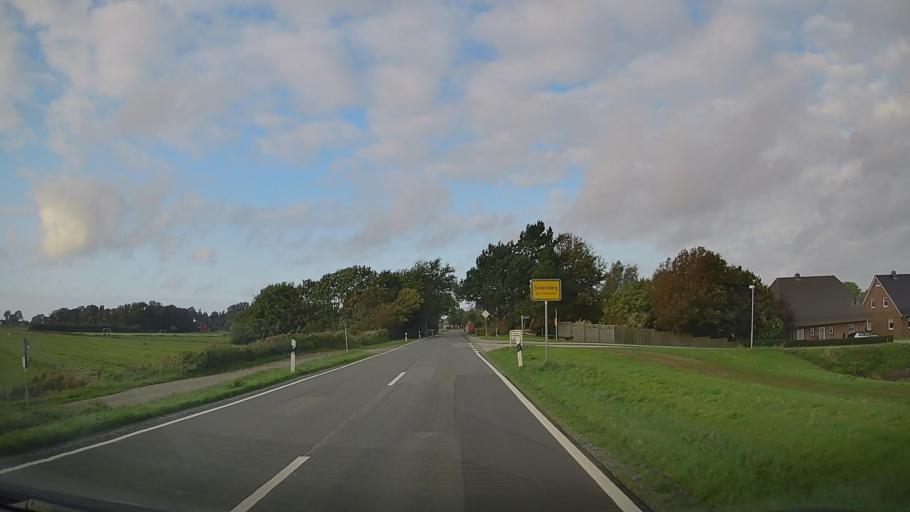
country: DE
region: Schleswig-Holstein
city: Simonsberg
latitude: 54.4315
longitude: 8.9753
